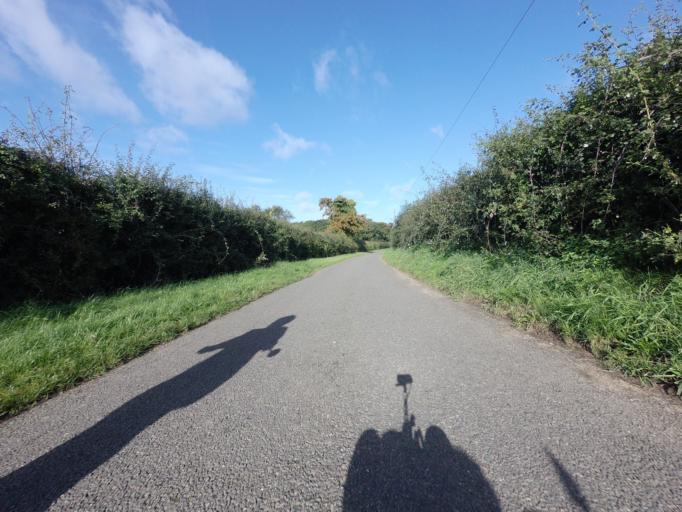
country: GB
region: England
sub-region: Norfolk
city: Dersingham
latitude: 52.8490
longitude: 0.6725
